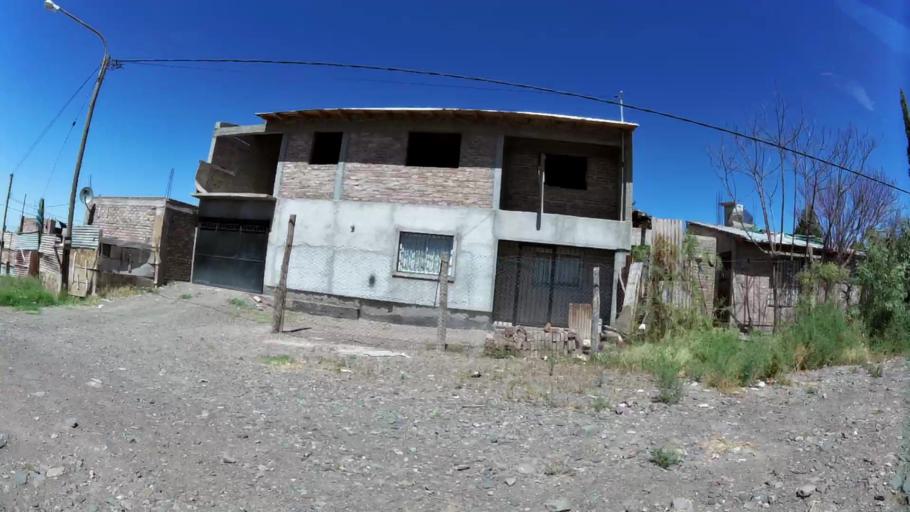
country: AR
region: Mendoza
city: Las Heras
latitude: -32.8513
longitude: -68.8664
